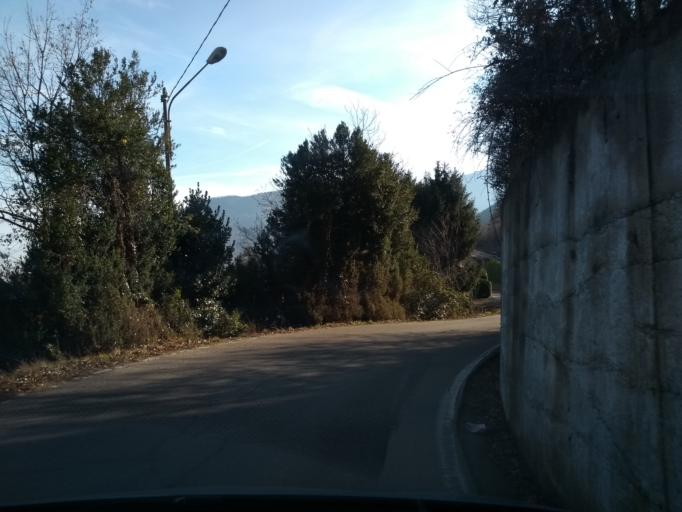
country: IT
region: Piedmont
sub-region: Provincia di Torino
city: Coassolo Torinese
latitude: 45.2809
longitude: 7.4616
